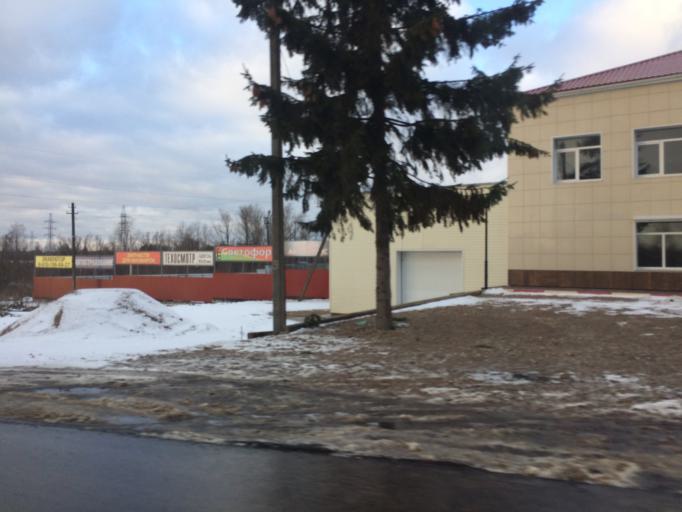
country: RU
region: Tula
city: Suvorov
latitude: 54.1329
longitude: 36.4750
